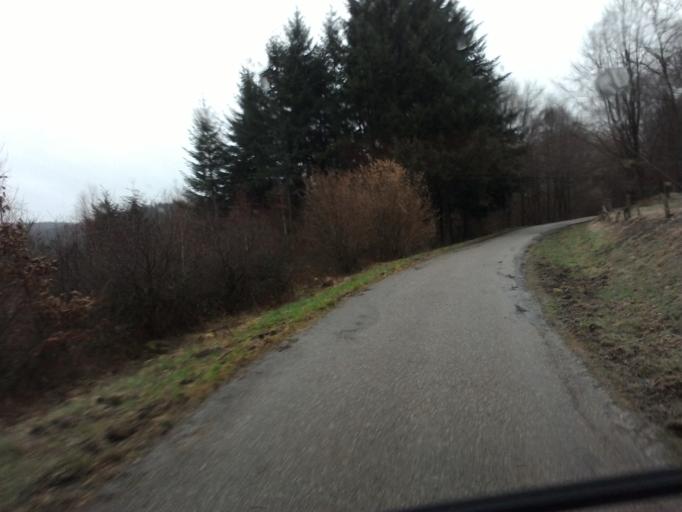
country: FR
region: Champagne-Ardenne
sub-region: Departement des Ardennes
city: Fromelennes
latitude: 50.0333
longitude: 4.8532
